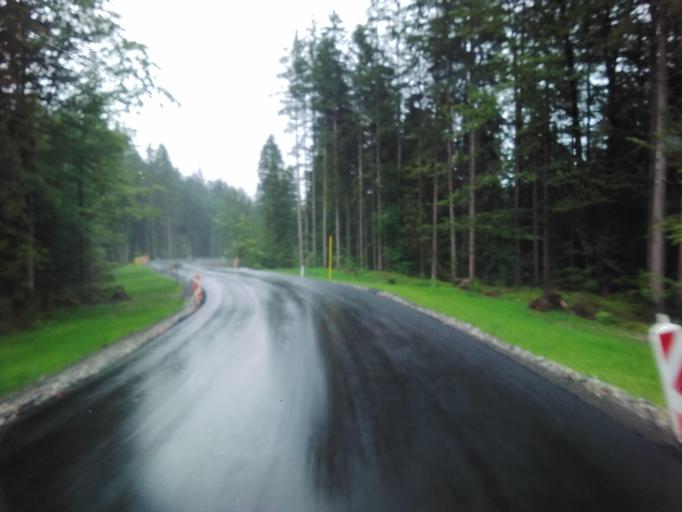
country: AT
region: Tyrol
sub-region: Politischer Bezirk Kitzbuhel
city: Schwendt
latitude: 47.5917
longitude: 12.3819
